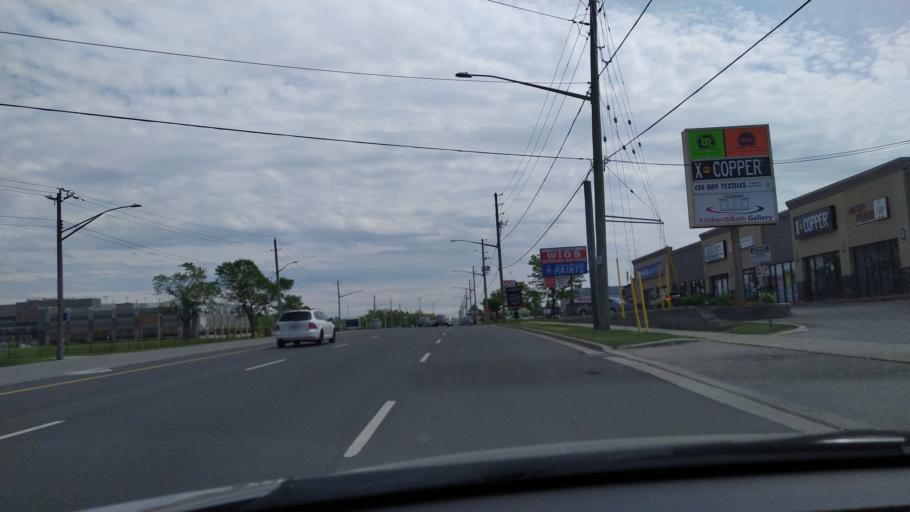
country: CA
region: Ontario
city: London
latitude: 42.9569
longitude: -81.2300
